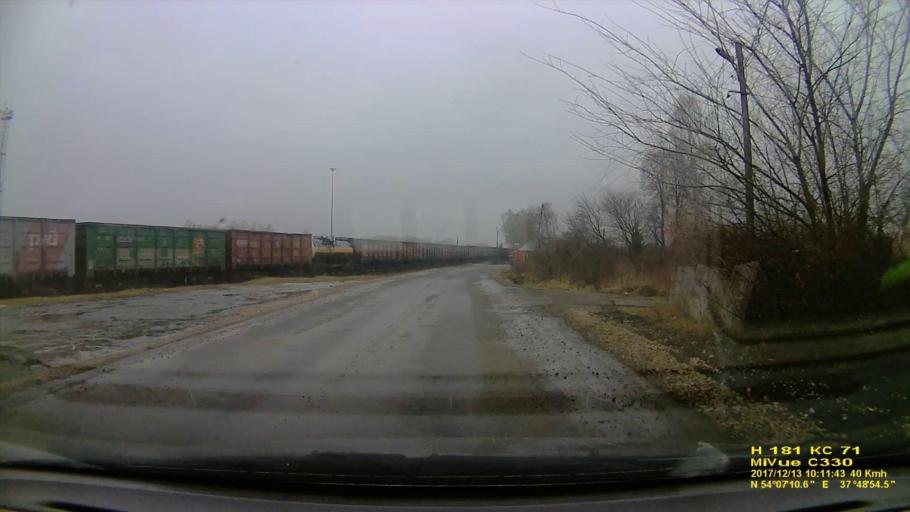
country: RU
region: Tula
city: Bolokhovo
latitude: 54.1196
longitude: 37.8148
